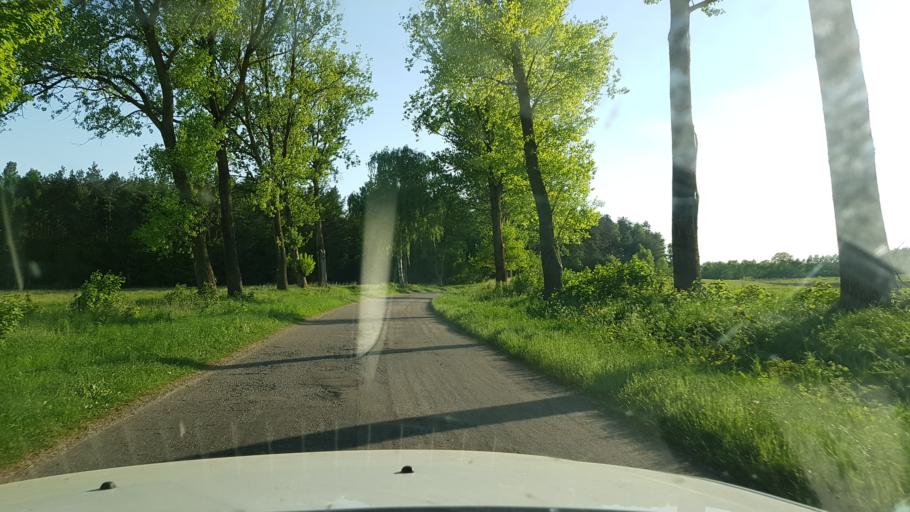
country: PL
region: West Pomeranian Voivodeship
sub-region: Powiat lobeski
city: Dobra
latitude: 53.6226
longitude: 15.3500
